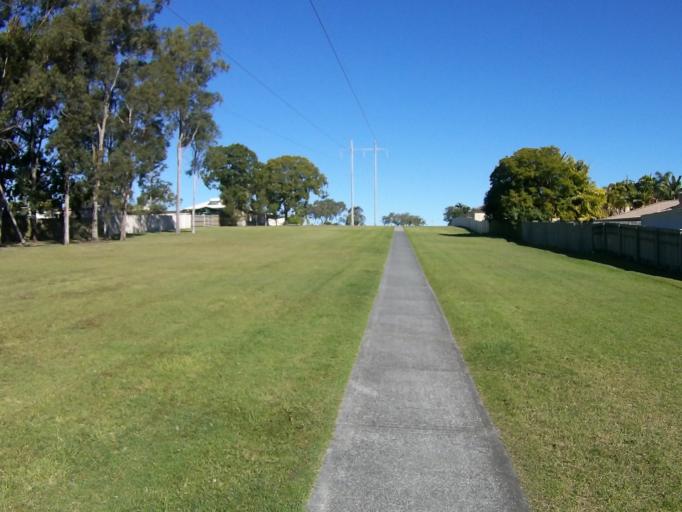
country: AU
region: Queensland
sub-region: Logan
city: Windaroo
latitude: -27.7406
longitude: 153.1935
